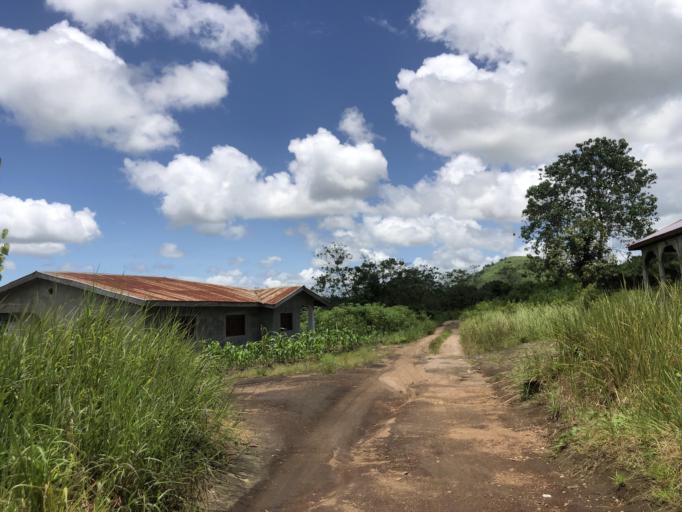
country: SL
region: Northern Province
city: Makeni
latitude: 8.8517
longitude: -12.0623
